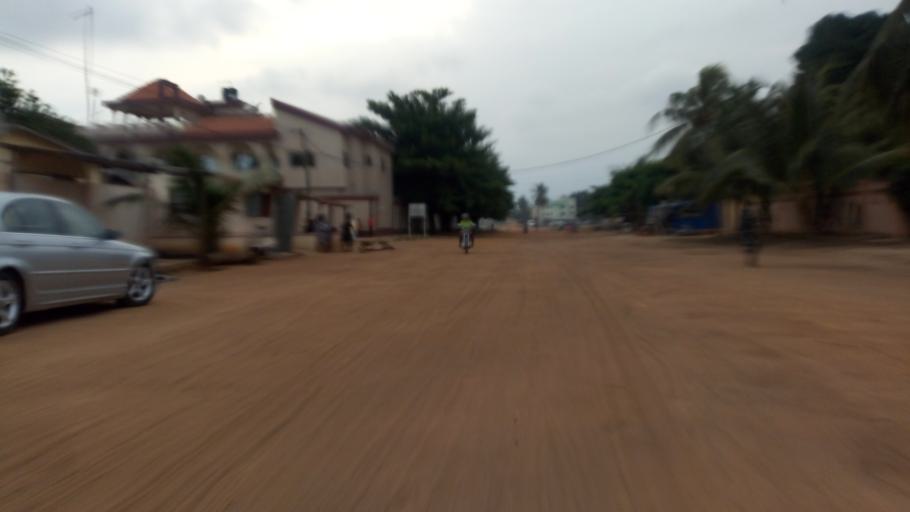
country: TG
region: Maritime
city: Lome
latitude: 6.1786
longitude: 1.1949
